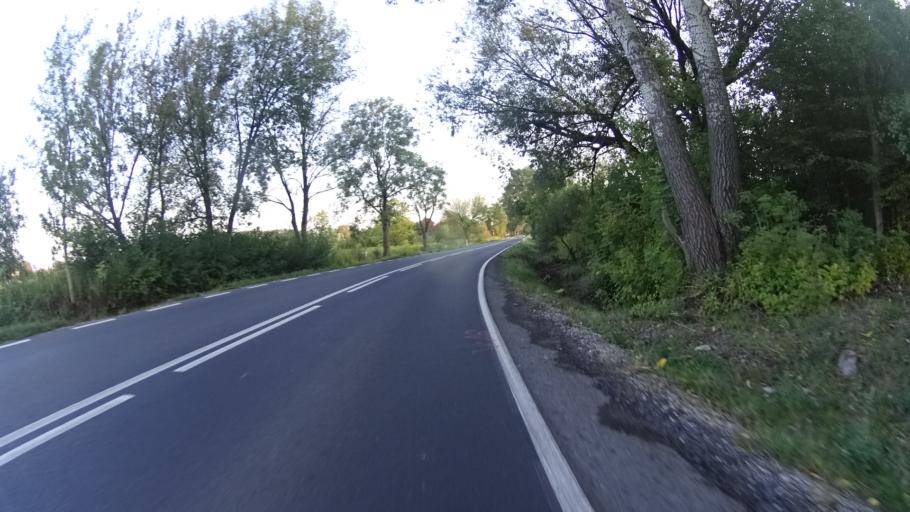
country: PL
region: Masovian Voivodeship
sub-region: Powiat warszawski zachodni
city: Ozarow Mazowiecki
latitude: 52.2233
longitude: 20.7741
